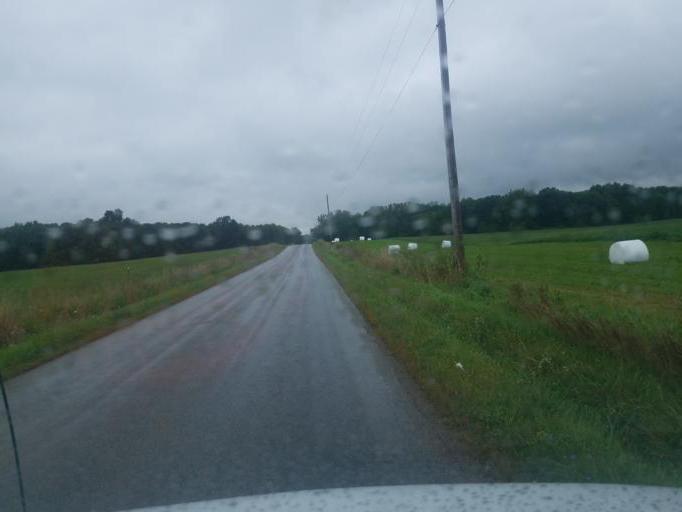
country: US
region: Ohio
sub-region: Wayne County
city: West Salem
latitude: 40.9354
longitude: -82.0862
